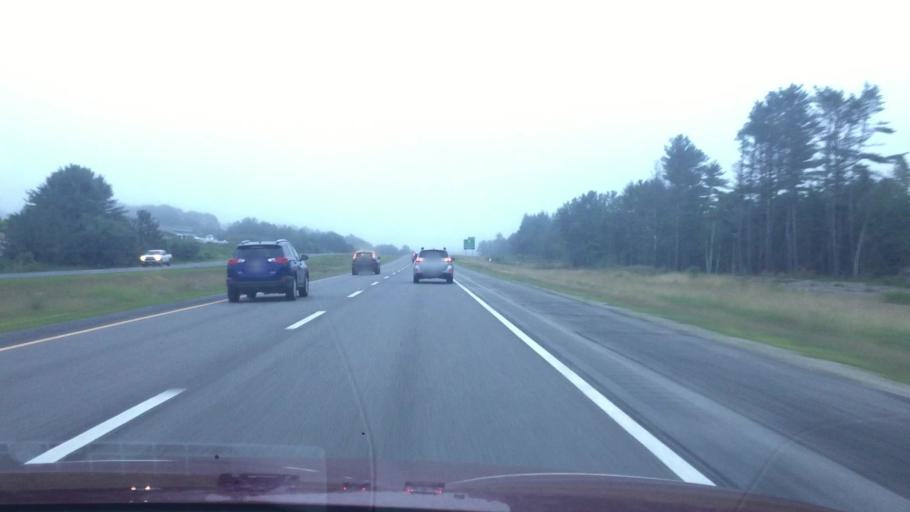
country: US
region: Maine
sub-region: Cumberland County
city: Yarmouth
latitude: 43.8208
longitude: -70.1442
